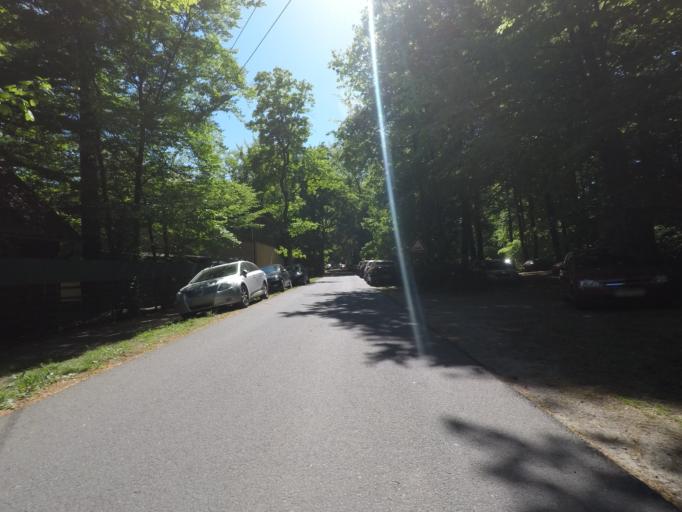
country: DE
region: Brandenburg
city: Eberswalde
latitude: 52.8234
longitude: 13.7803
